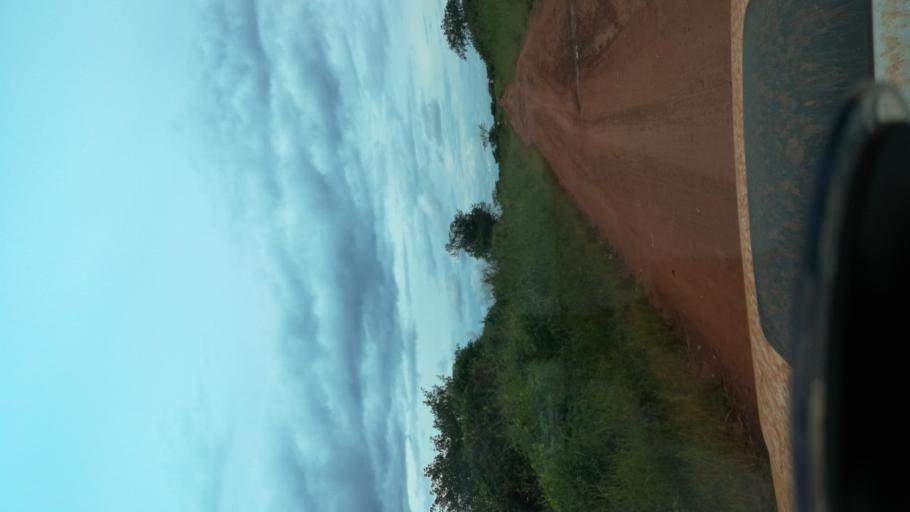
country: ZM
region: Luapula
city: Nchelenge
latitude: -9.2133
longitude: 28.2810
